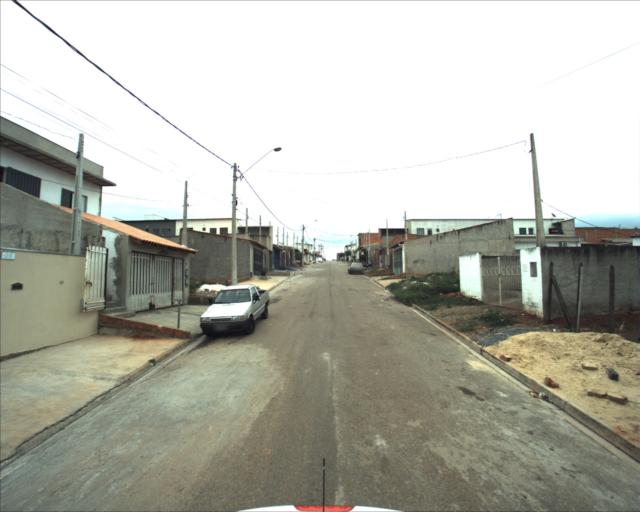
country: BR
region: Sao Paulo
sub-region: Sorocaba
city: Sorocaba
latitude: -23.4318
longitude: -47.5010
